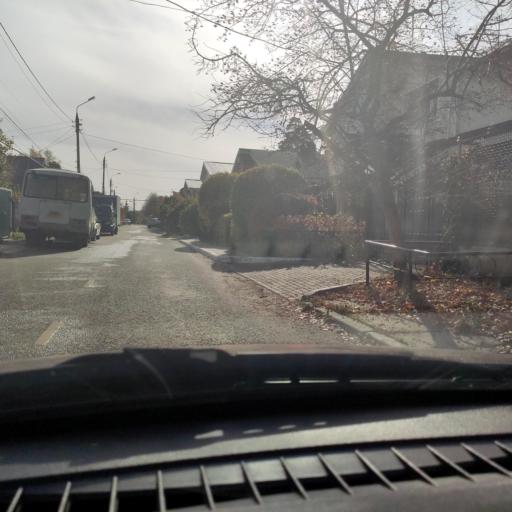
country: RU
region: Samara
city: Tol'yatti
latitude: 53.5363
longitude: 49.3876
